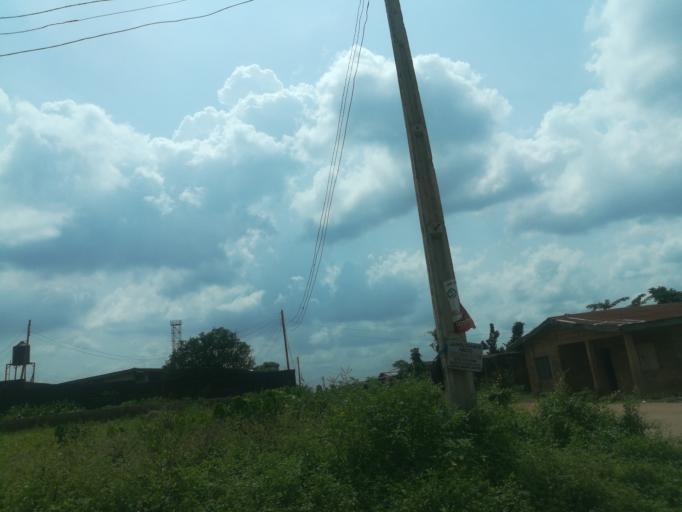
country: NG
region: Oyo
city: Ibadan
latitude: 7.4378
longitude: 3.9385
